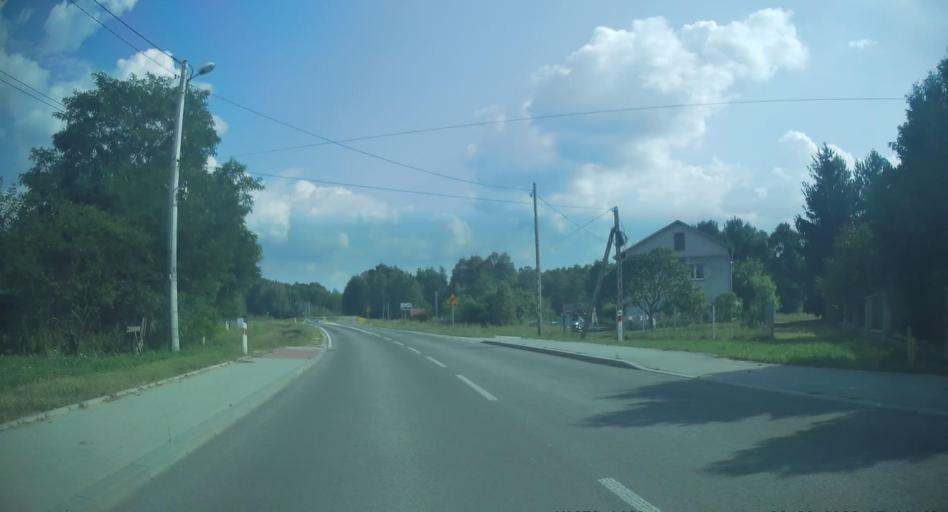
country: PL
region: Swietokrzyskie
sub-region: Powiat konecki
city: Radoszyce
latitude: 51.0620
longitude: 20.2755
